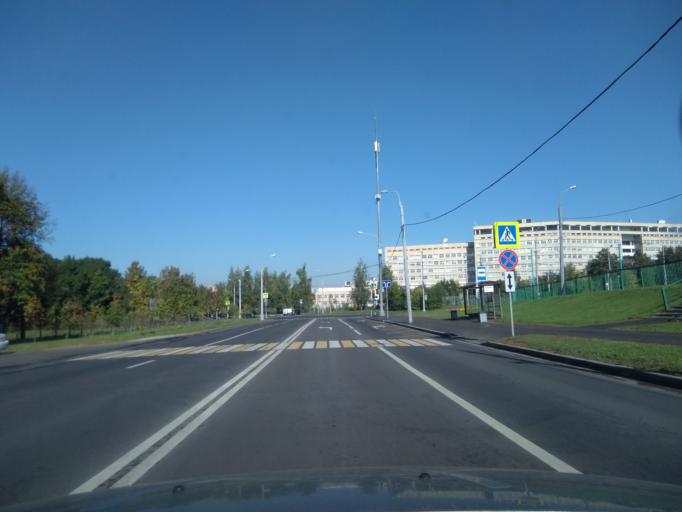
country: RU
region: Moscow
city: Strogino
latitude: 55.8495
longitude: 37.4029
